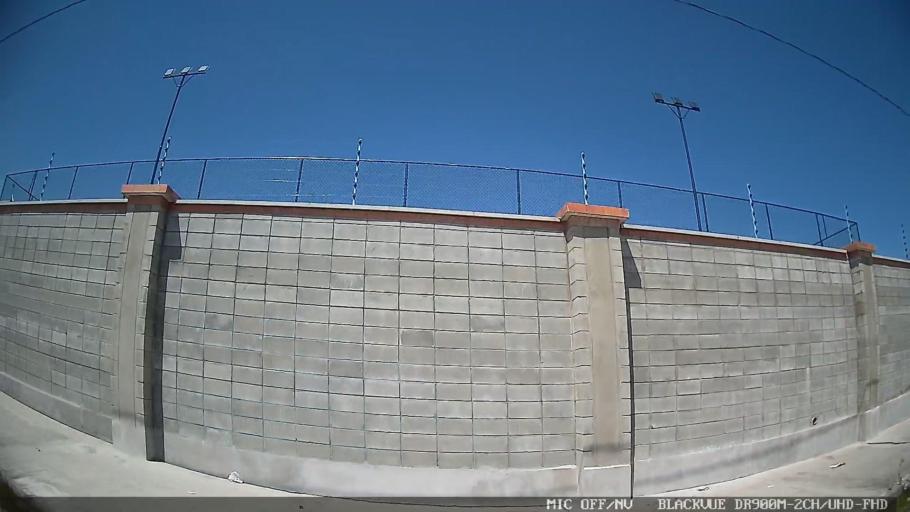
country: BR
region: Sao Paulo
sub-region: Peruibe
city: Peruibe
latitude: -24.3022
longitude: -46.9972
